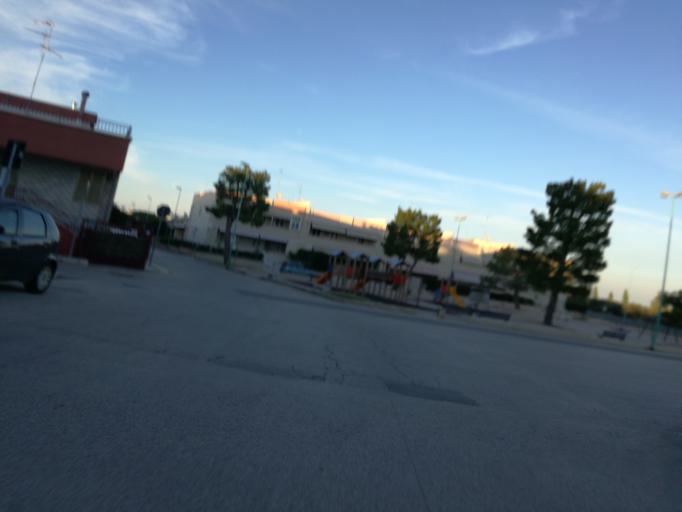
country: IT
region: Apulia
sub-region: Provincia di Bari
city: Adelfia
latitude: 41.0023
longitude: 16.8810
